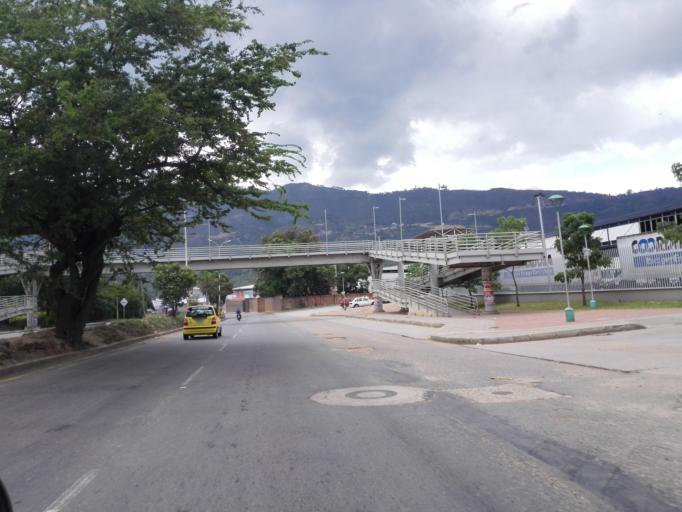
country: CO
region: Santander
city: Giron
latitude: 7.0851
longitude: -73.1648
